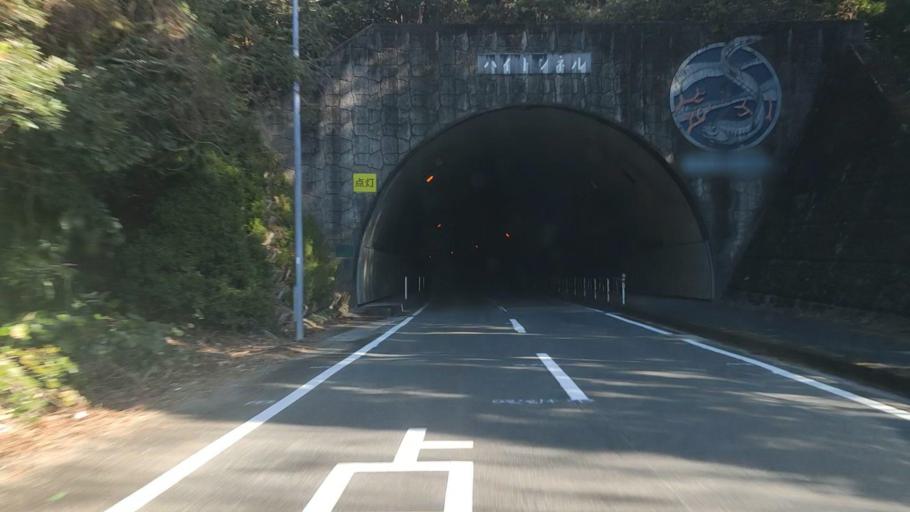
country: JP
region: Miyazaki
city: Nobeoka
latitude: 32.6977
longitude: 131.8135
